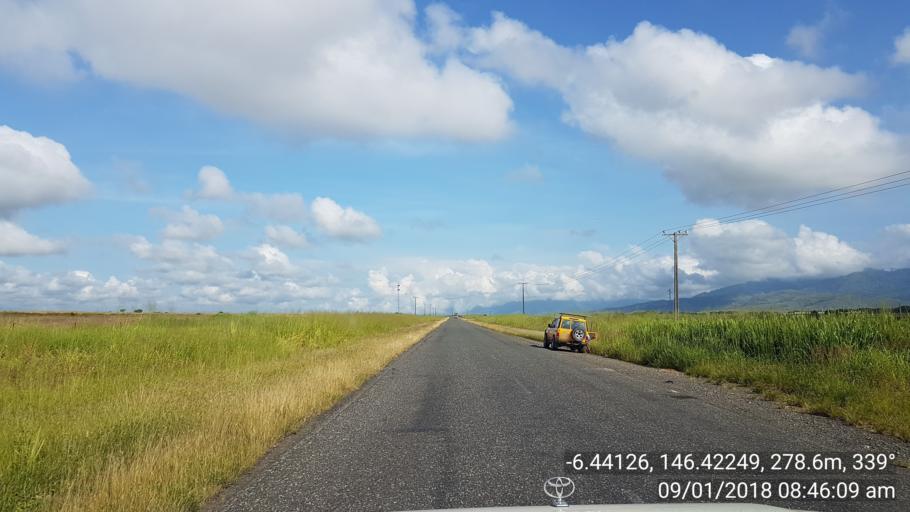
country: PG
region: Eastern Highlands
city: Kainantu
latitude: -6.4414
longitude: 146.4225
